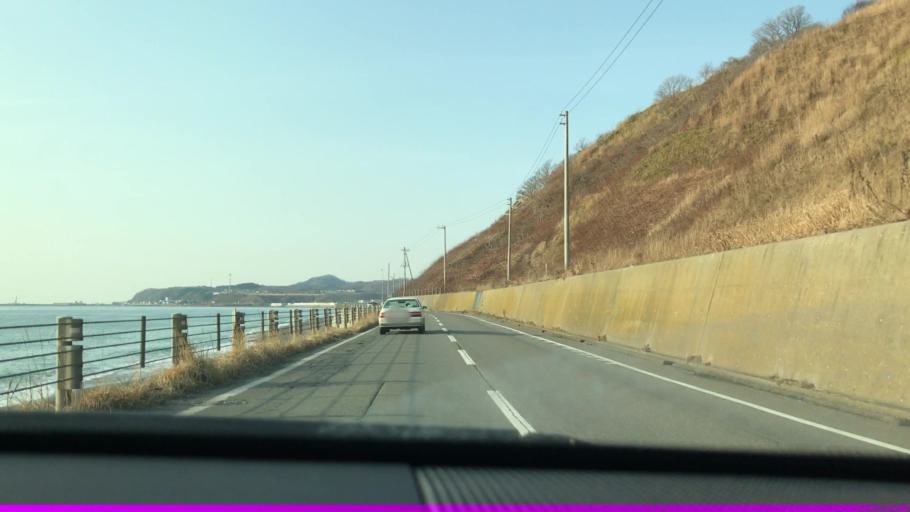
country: JP
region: Hokkaido
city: Shizunai-furukawacho
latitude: 42.2372
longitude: 142.5947
